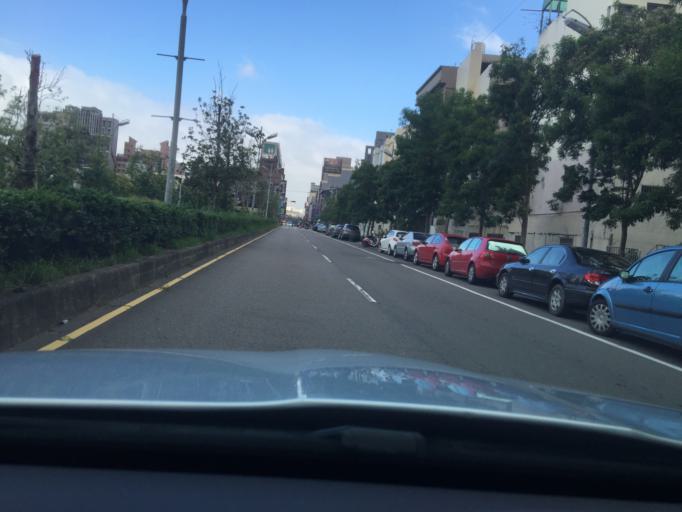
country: TW
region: Taiwan
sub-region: Hsinchu
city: Zhubei
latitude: 24.8231
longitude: 121.0074
